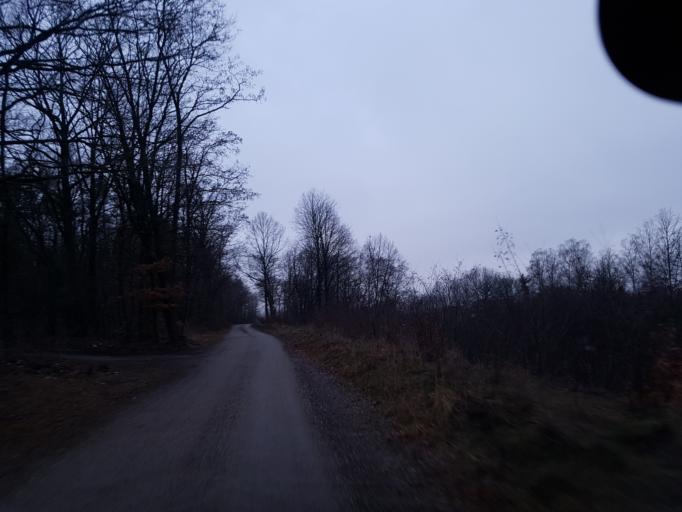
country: DE
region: Brandenburg
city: Hohenleipisch
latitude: 51.4954
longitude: 13.5709
